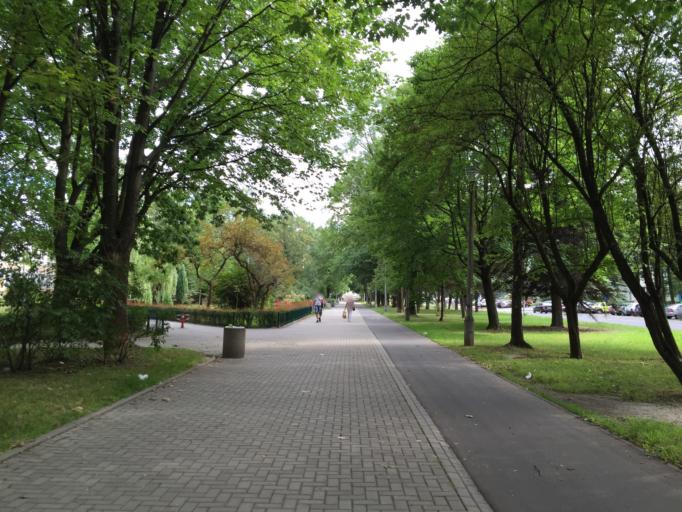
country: PL
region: Lesser Poland Voivodeship
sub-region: Powiat wielicki
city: Kokotow
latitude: 50.0750
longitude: 20.0302
